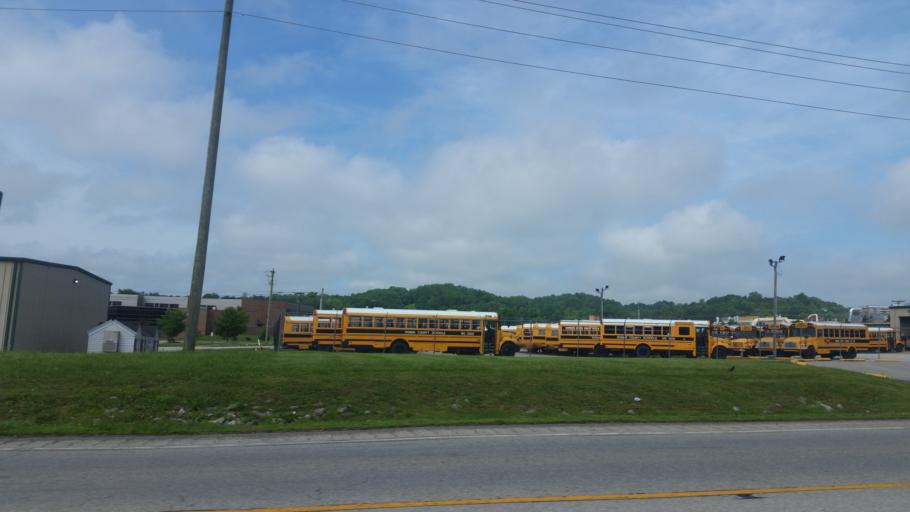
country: US
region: Kentucky
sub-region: Rowan County
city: Morehead
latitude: 38.2095
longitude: -83.4765
